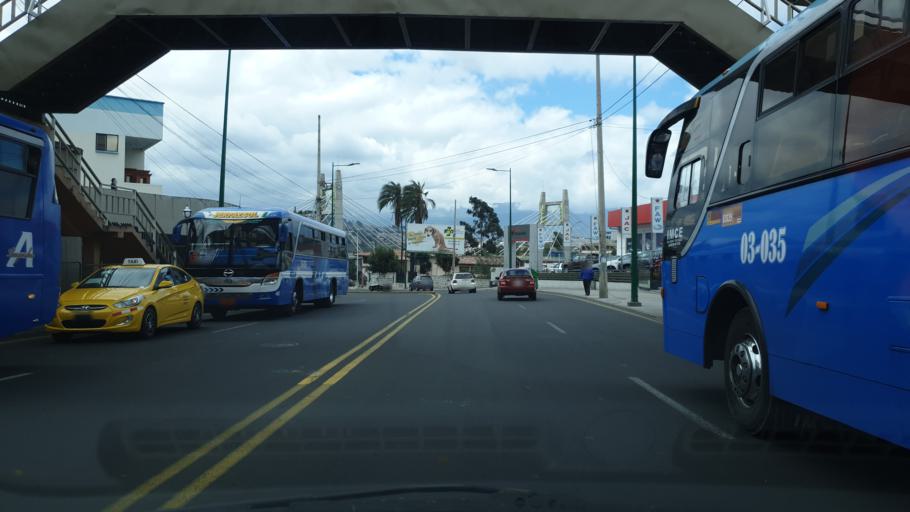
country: EC
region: Tungurahua
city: Ambato
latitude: -1.2342
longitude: -78.6307
